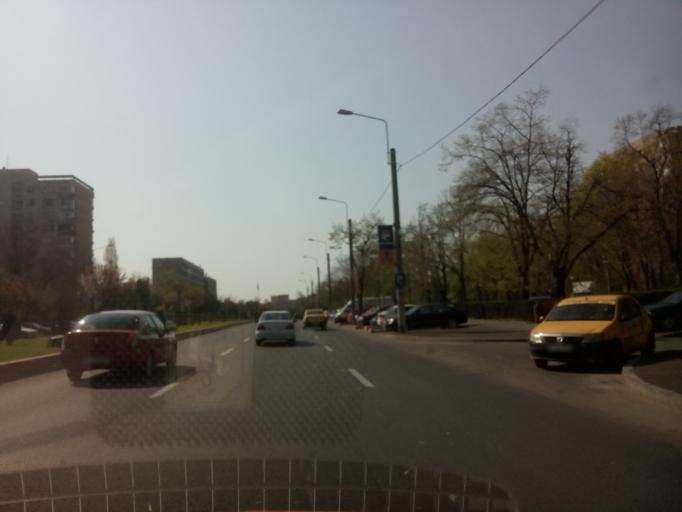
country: RO
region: Ilfov
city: Dobroesti
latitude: 44.4234
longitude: 26.1637
